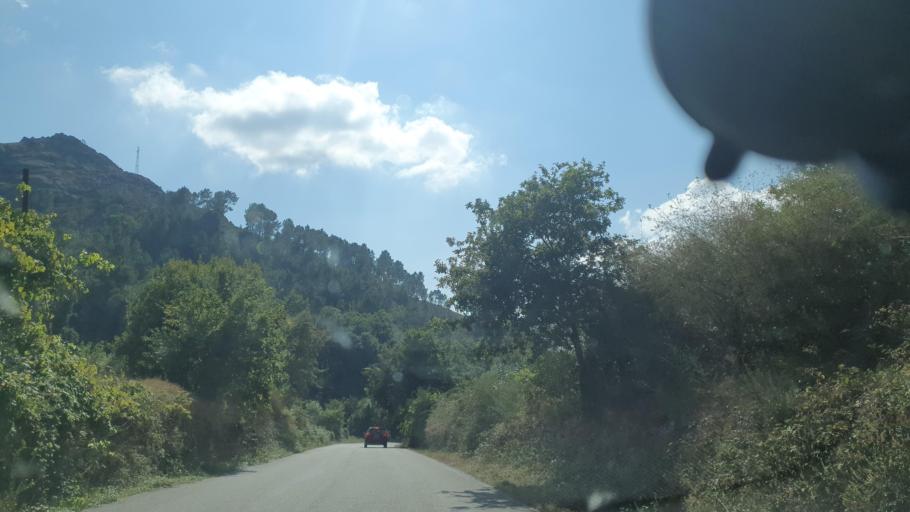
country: PT
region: Braga
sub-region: Terras de Bouro
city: Antas
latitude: 41.7634
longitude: -8.2007
